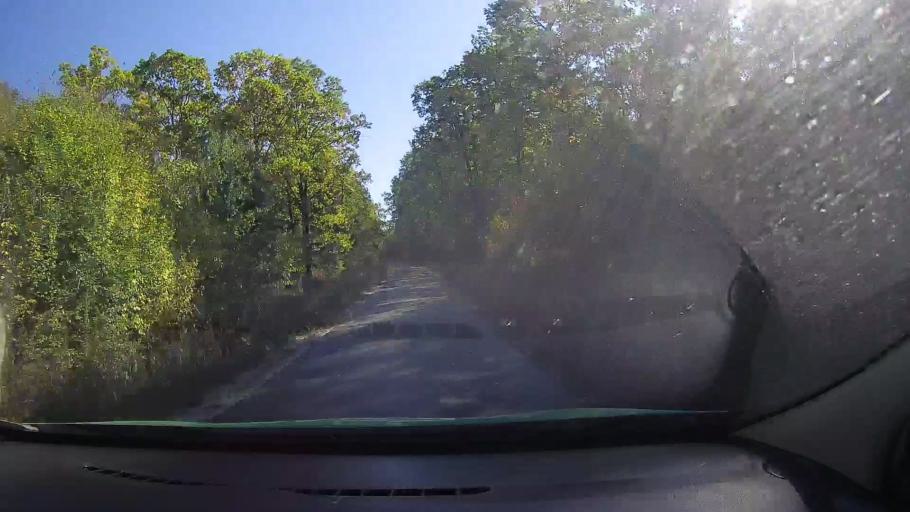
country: RO
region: Satu Mare
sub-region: Comuna Doba
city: Doba
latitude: 47.7101
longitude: 22.7527
